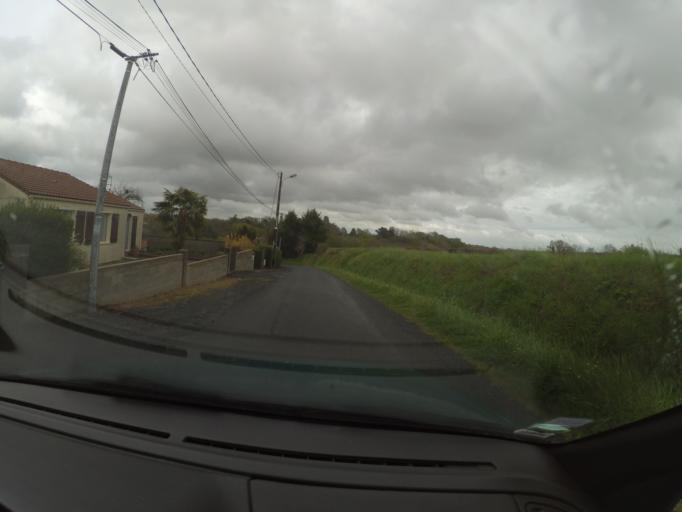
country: FR
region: Pays de la Loire
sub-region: Departement de la Loire-Atlantique
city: Monnieres
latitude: 47.1364
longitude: -1.3466
